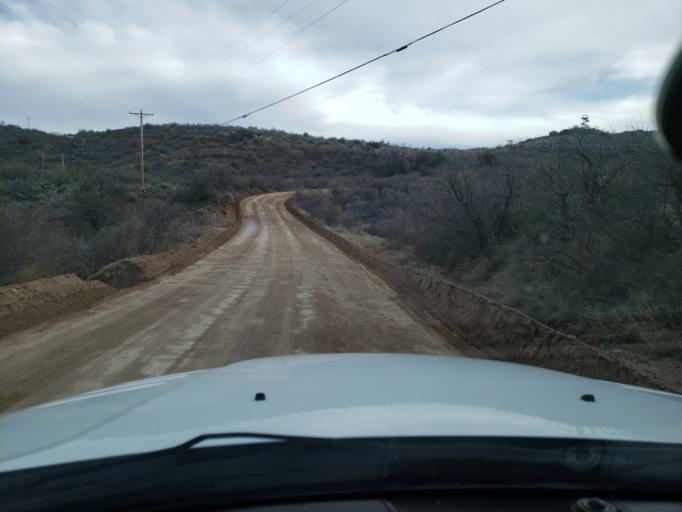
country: US
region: Arizona
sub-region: Pinal County
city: Oracle
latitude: 32.5517
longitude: -110.7082
